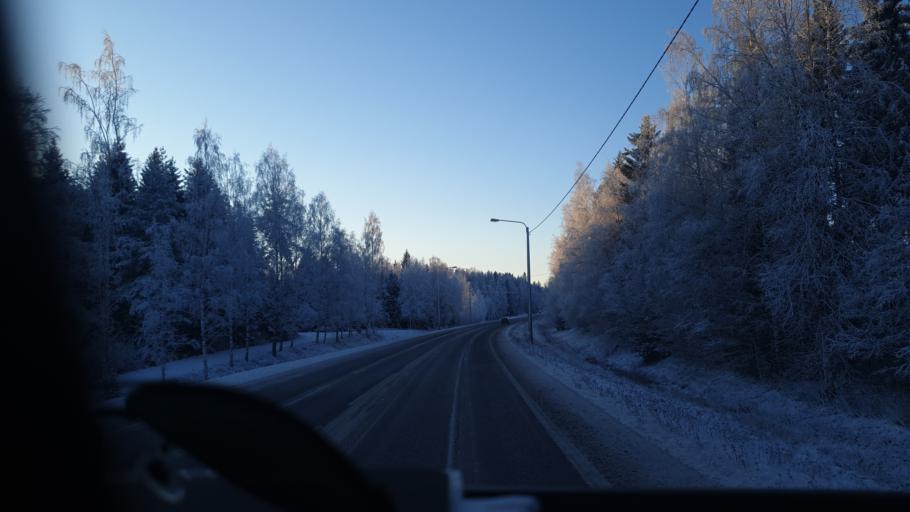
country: FI
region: Central Ostrobothnia
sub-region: Kokkola
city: Kaelviae
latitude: 63.9261
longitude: 23.4252
